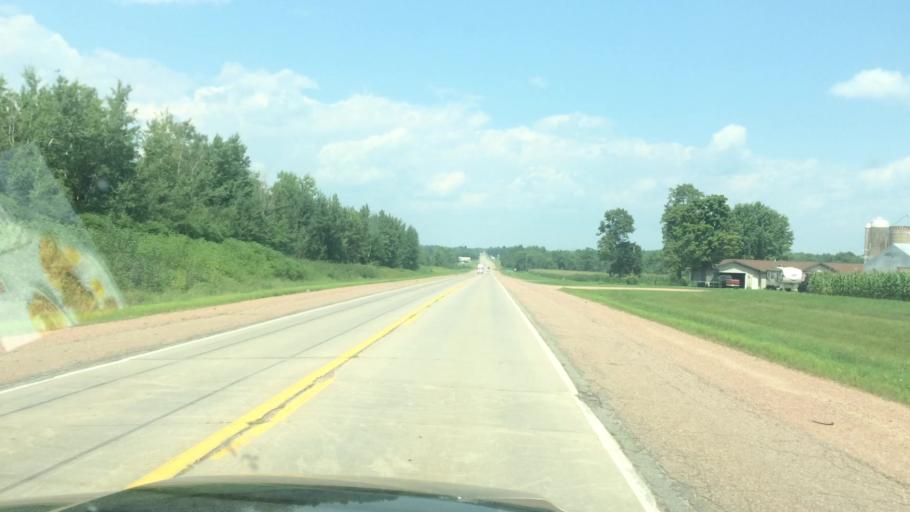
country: US
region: Wisconsin
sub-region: Clark County
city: Colby
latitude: 44.8828
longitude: -90.3155
